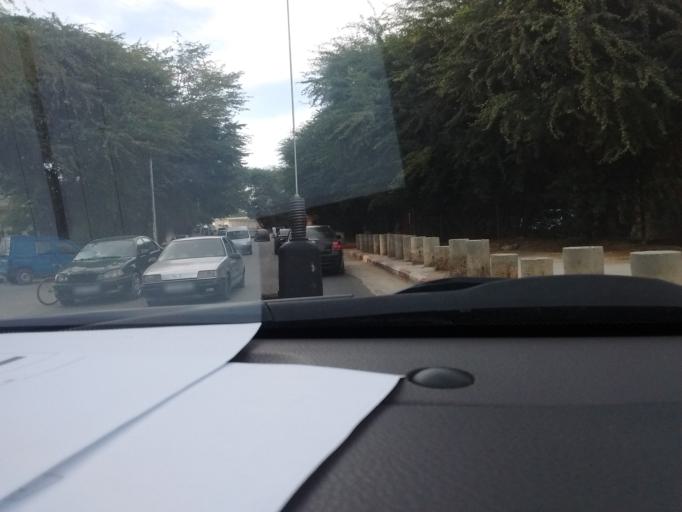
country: MR
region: Nouakchott
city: Nouakchott
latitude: 18.0925
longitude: -15.9835
